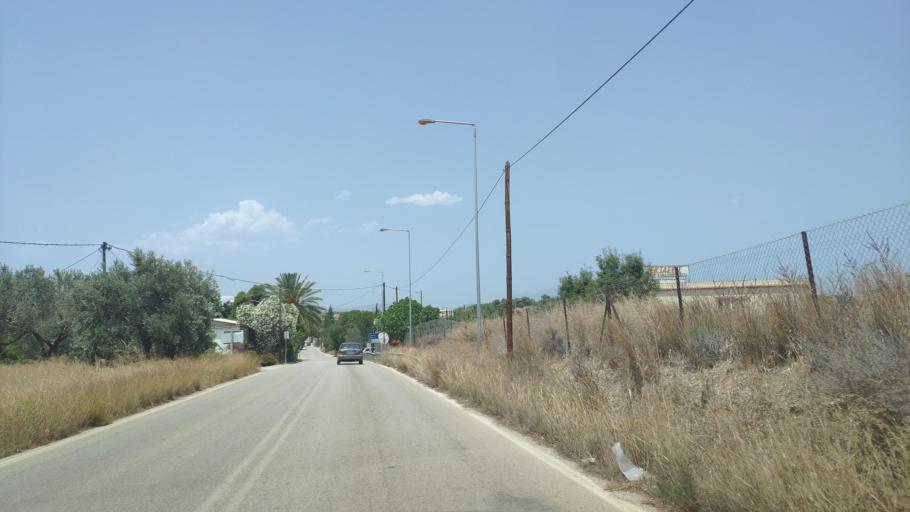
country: GR
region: Peloponnese
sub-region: Nomos Argolidos
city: Porto Cheli
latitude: 37.3155
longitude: 23.1584
